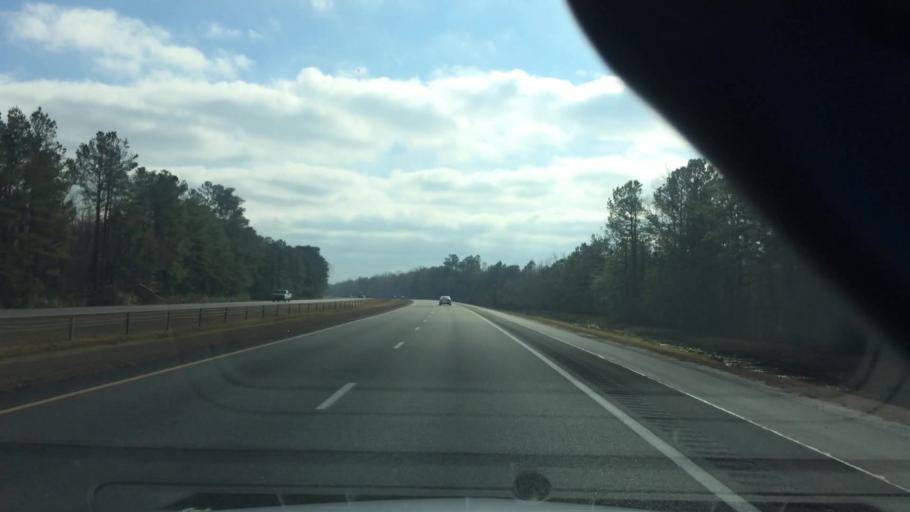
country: US
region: North Carolina
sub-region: Pender County
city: Rocky Point
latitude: 34.4651
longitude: -77.8803
